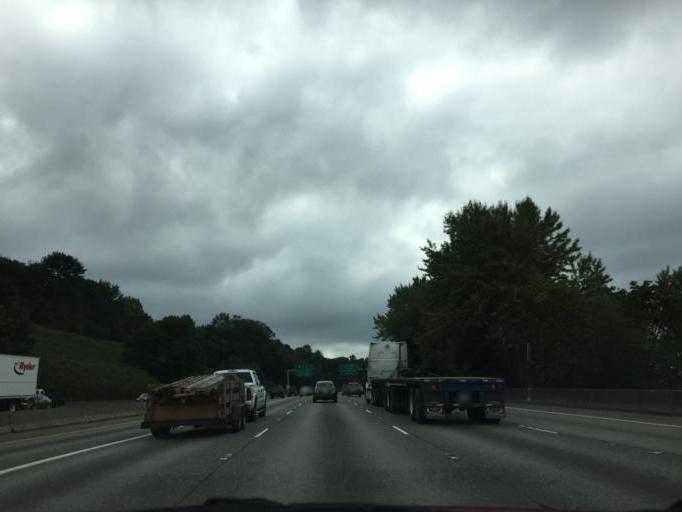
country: US
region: Washington
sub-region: King County
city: Tukwila
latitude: 47.4941
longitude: -122.2680
